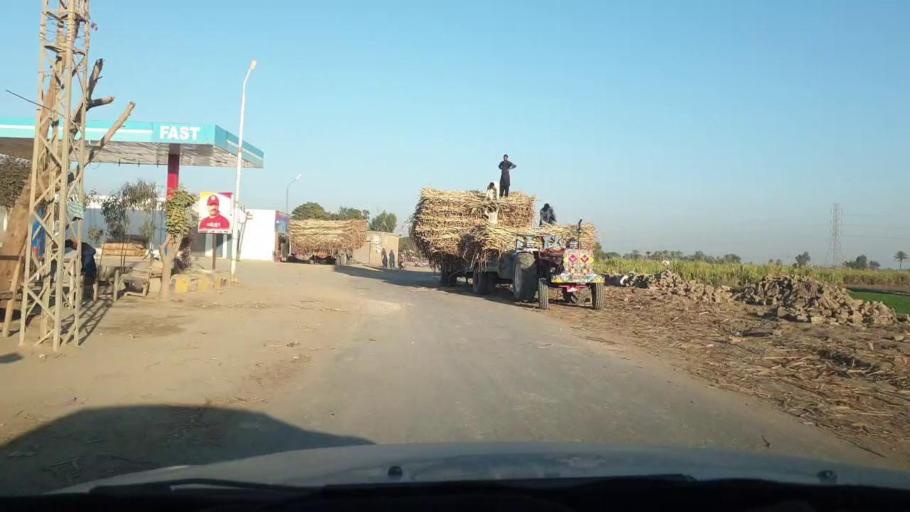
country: PK
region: Sindh
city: Ghotki
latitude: 27.9942
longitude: 69.2724
